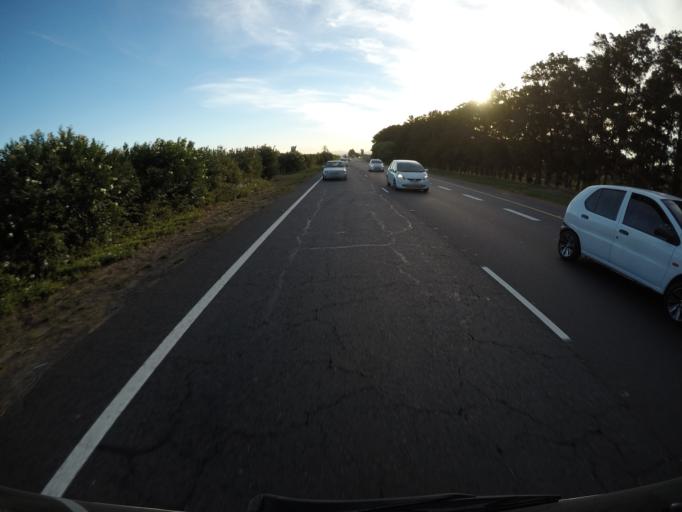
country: ZA
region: Western Cape
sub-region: City of Cape Town
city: Kraaifontein
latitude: -33.8259
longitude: 18.7698
